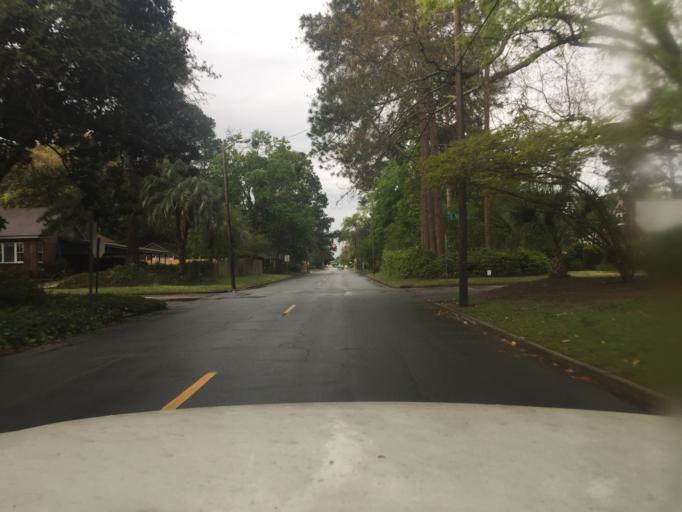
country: US
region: Georgia
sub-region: Chatham County
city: Thunderbolt
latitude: 32.0377
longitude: -81.0934
